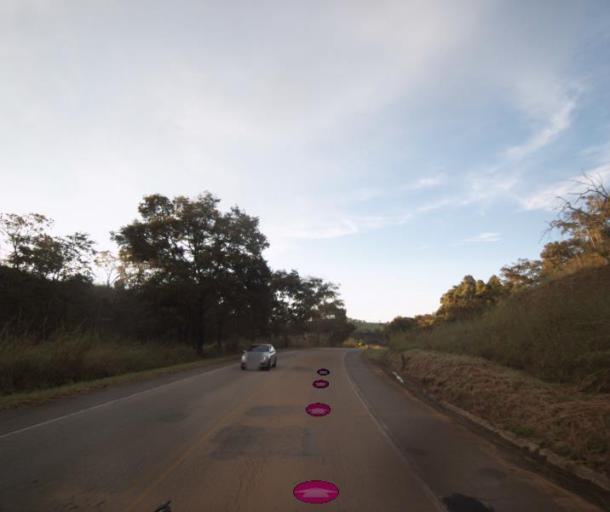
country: BR
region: Goias
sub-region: Abadiania
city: Abadiania
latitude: -16.1283
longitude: -48.8949
